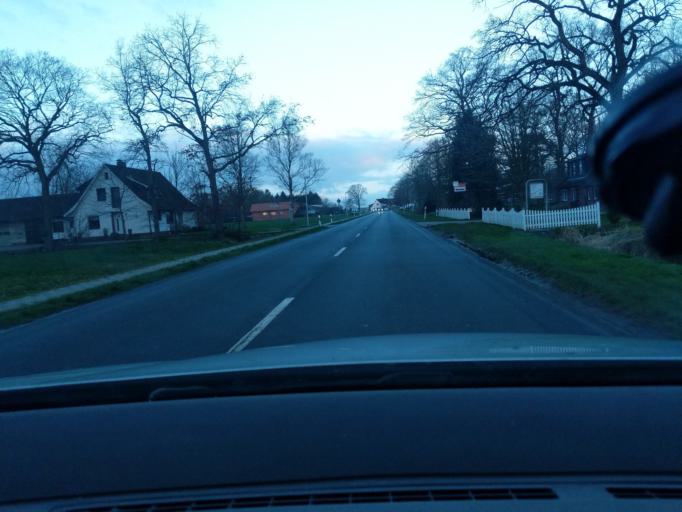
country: DE
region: Lower Saxony
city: Stinstedt
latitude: 53.6348
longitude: 8.9644
